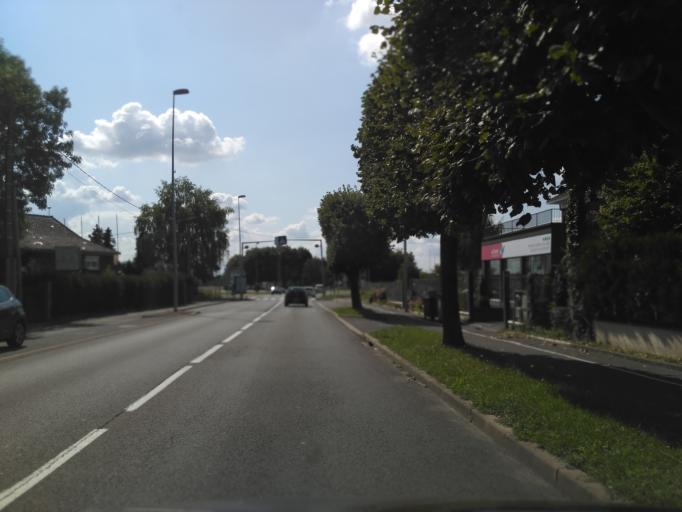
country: FR
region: Ile-de-France
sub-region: Departement de Seine-et-Marne
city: Le Mee-sur-Seine
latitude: 48.5070
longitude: 2.6099
